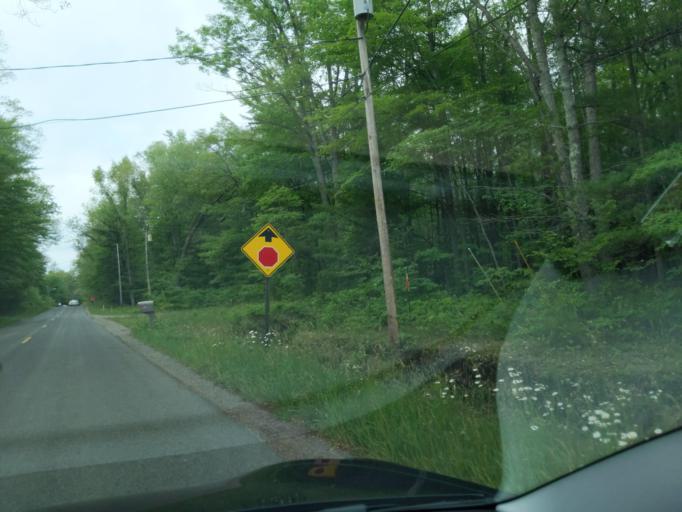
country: US
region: Michigan
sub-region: Muskegon County
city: North Muskegon
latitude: 43.2618
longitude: -86.3223
